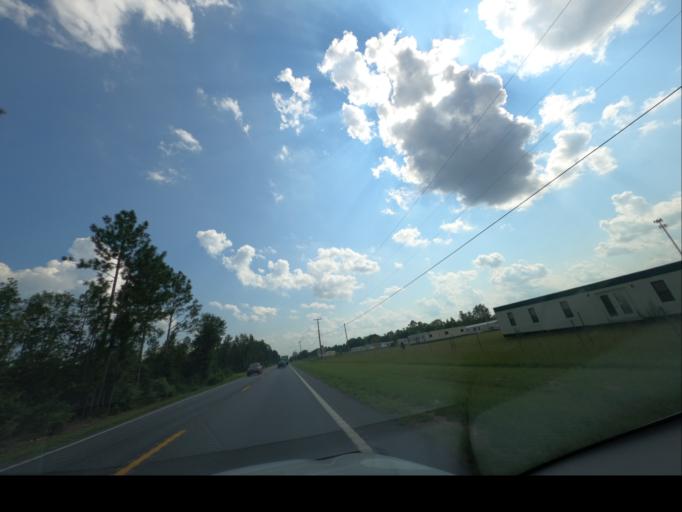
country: US
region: South Carolina
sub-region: Lexington County
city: Red Bank
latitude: 33.8206
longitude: -81.2201
